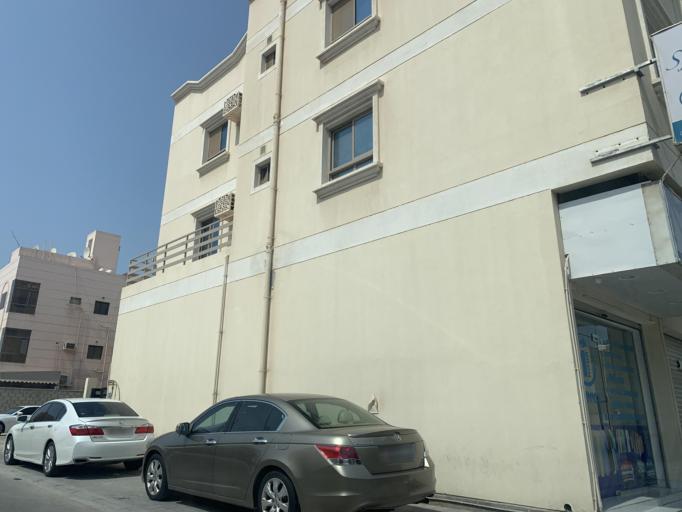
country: BH
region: Muharraq
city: Al Hadd
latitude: 26.2649
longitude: 50.6560
